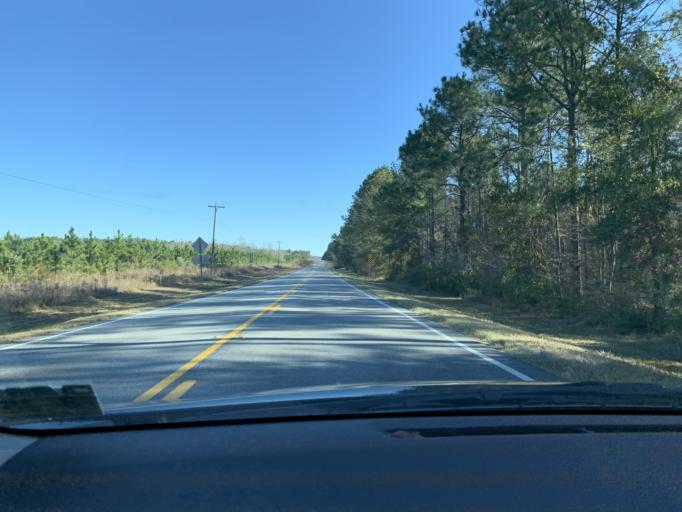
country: US
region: Georgia
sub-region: Ben Hill County
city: Fitzgerald
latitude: 31.7603
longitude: -83.1186
